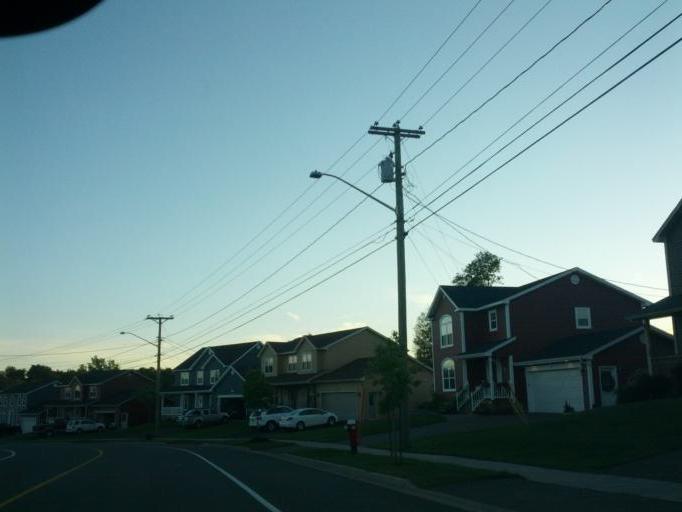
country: CA
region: New Brunswick
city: Moncton
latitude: 46.1093
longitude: -64.8699
